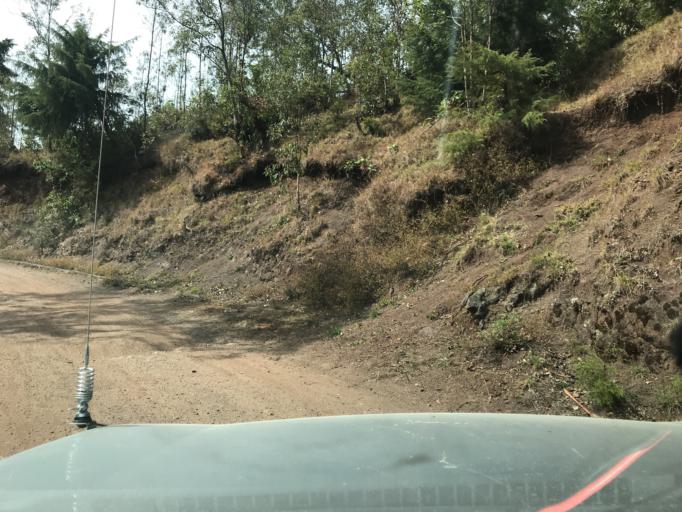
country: TL
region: Ainaro
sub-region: Ainaro
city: Ainaro
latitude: -8.8817
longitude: 125.5389
